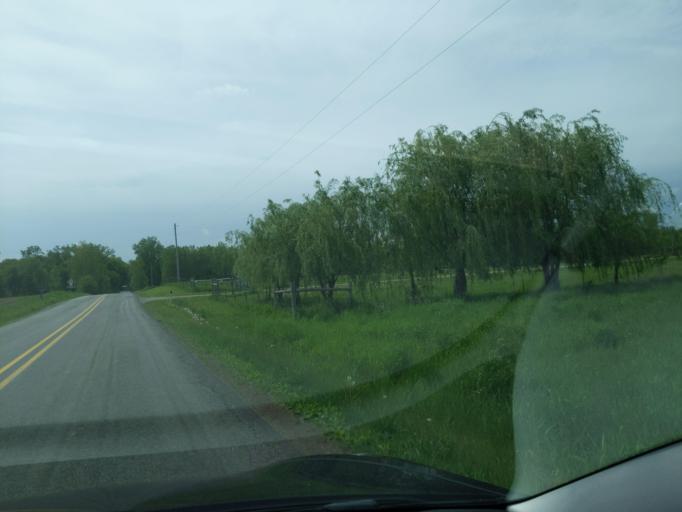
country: US
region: Michigan
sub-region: Ingham County
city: Stockbridge
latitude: 42.4247
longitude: -84.2783
